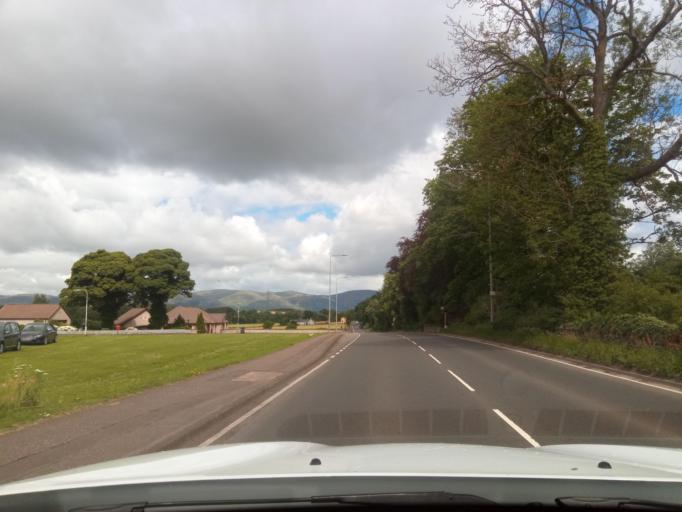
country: GB
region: Scotland
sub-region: Fife
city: Kincardine
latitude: 56.0790
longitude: -3.7203
